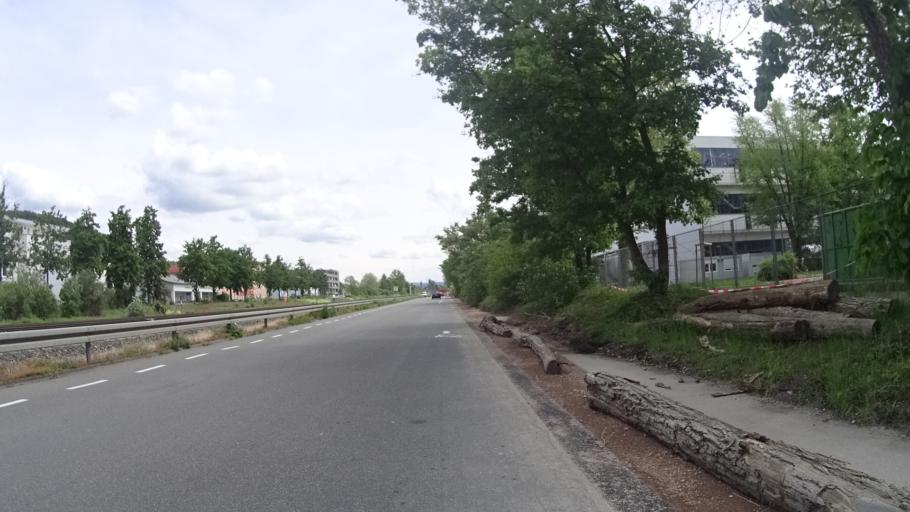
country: CH
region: Basel-City
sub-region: Basel-Stadt
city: Bettingen
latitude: 47.5505
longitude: 7.6612
